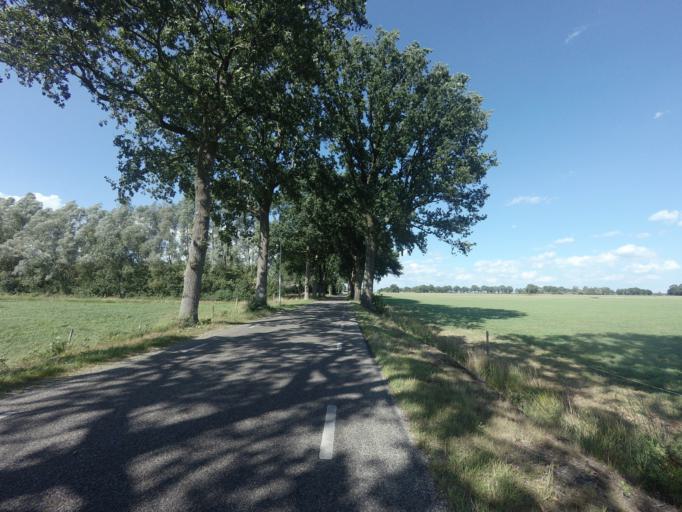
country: NL
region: Drenthe
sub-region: Gemeente Hoogeveen
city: Hoogeveen
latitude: 52.6280
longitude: 6.4833
